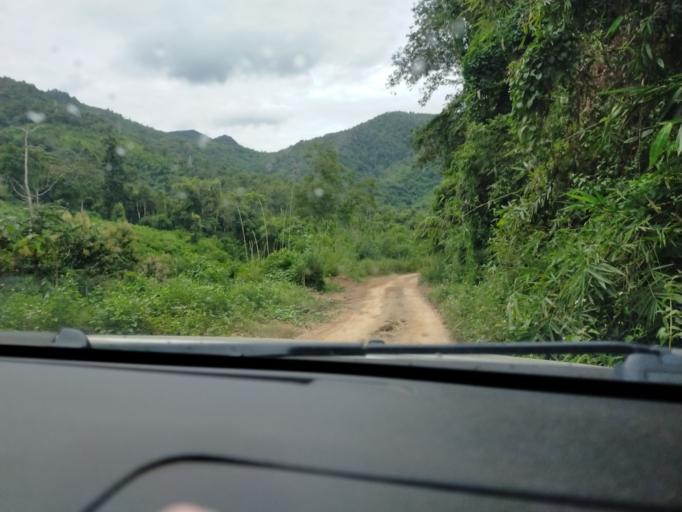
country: TH
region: Nan
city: Chaloem Phra Kiat
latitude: 19.8114
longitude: 101.3619
